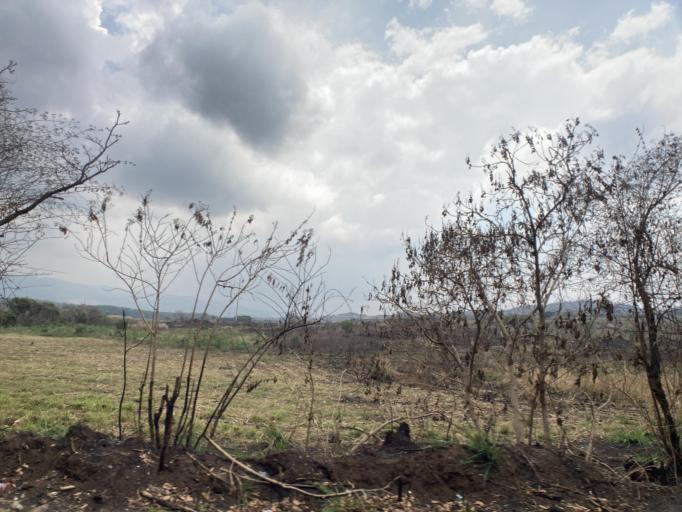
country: GT
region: Guatemala
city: Fraijanes
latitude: 14.3825
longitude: -90.4888
